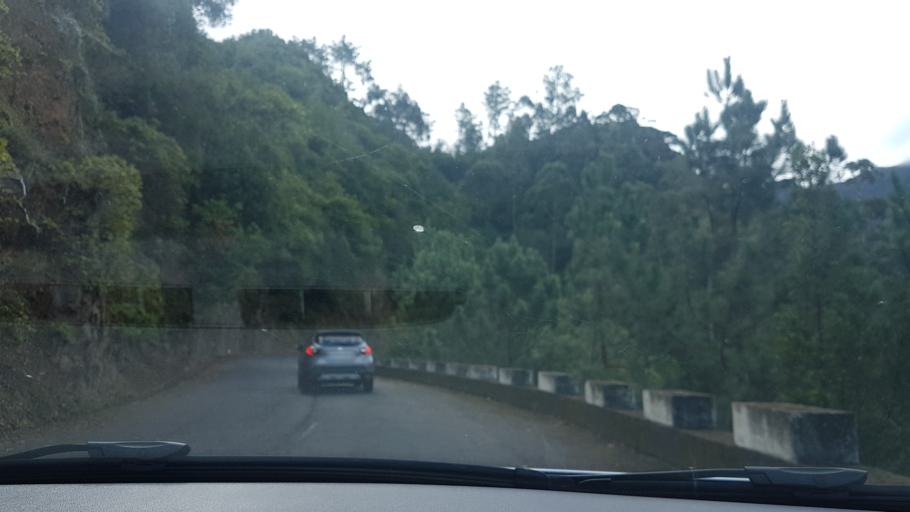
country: PT
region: Madeira
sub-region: Sao Vicente
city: Sao Vicente
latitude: 32.7719
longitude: -17.0266
